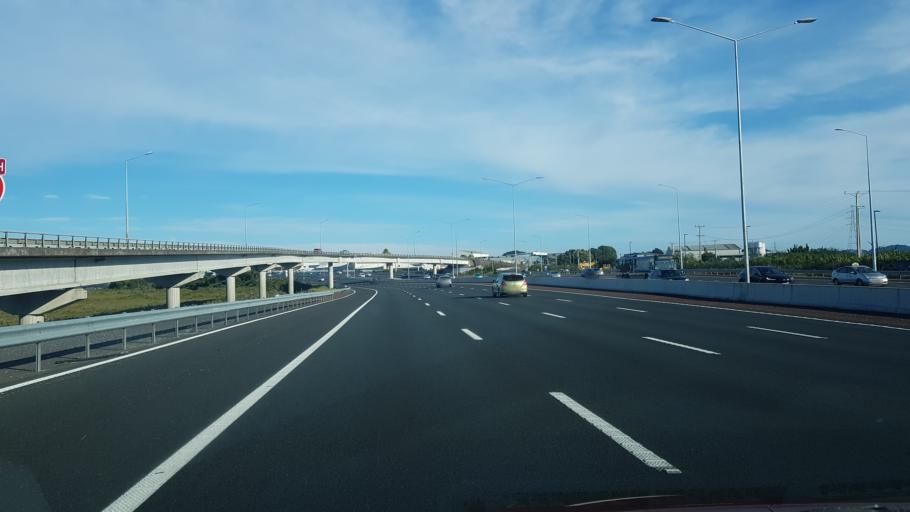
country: NZ
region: Auckland
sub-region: Auckland
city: Rosebank
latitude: -36.8632
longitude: 174.6648
